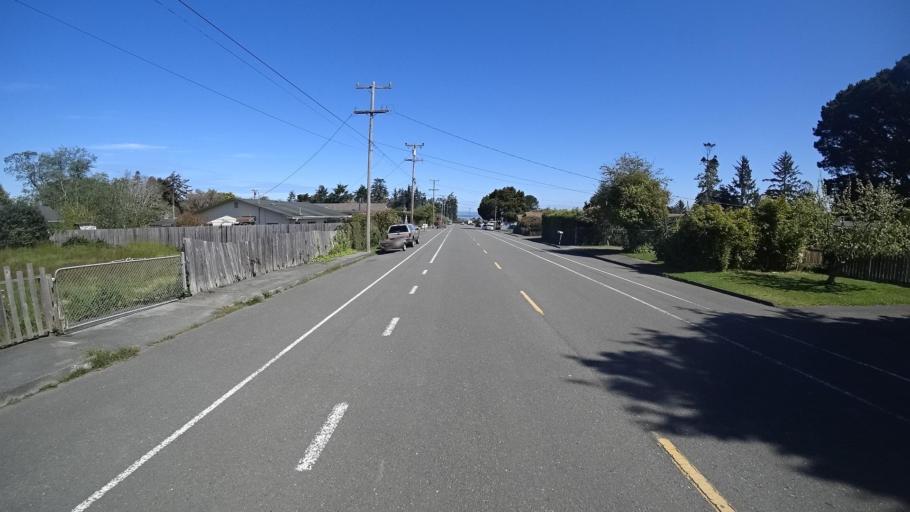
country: US
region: California
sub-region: Humboldt County
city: Myrtletown
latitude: 40.7925
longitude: -124.1262
